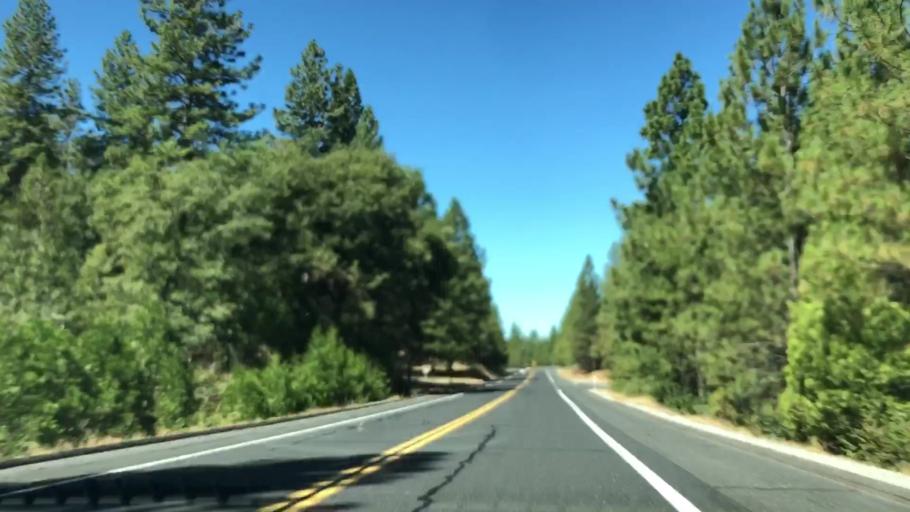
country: US
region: California
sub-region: Tuolumne County
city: Tuolumne City
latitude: 37.8279
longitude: -120.1808
